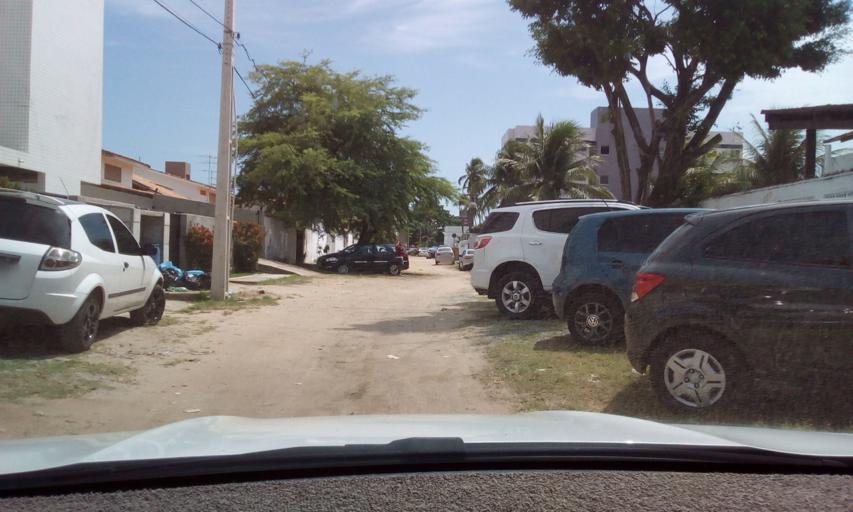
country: BR
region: Paraiba
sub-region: Cabedelo
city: Cabedelo
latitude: -7.0154
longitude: -34.8298
